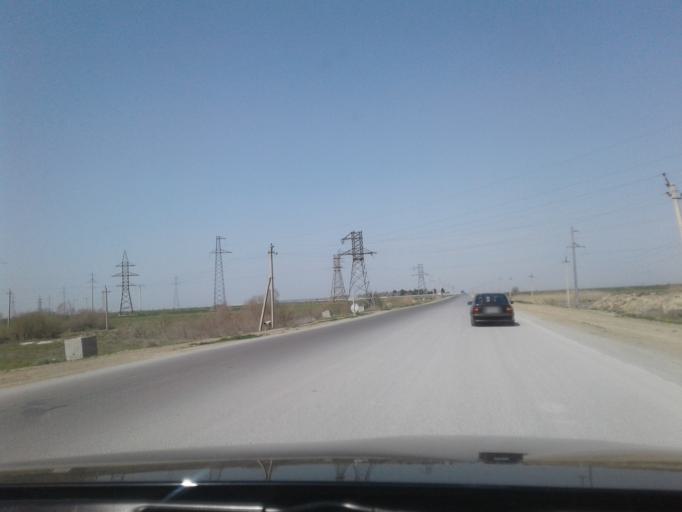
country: TM
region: Ahal
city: Abadan
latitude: 38.1785
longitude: 57.9788
